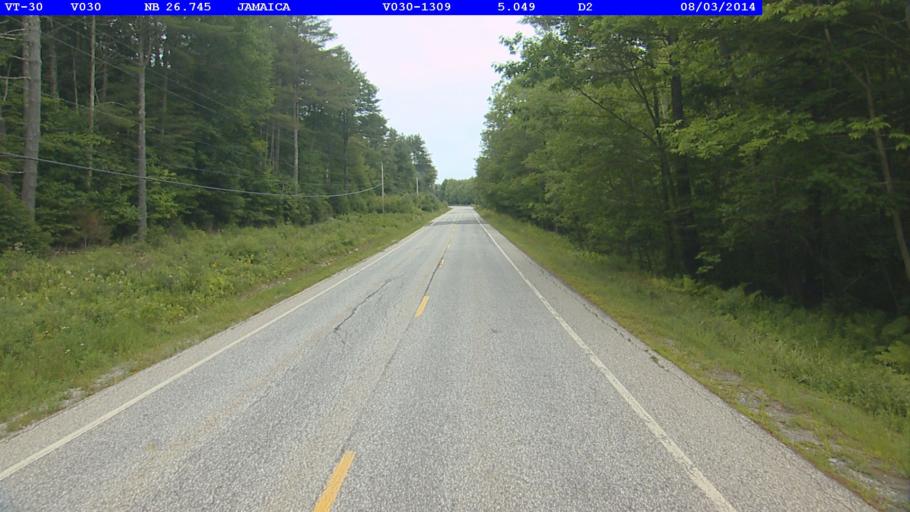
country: US
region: Vermont
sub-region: Windham County
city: Dover
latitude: 43.1073
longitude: -72.7955
